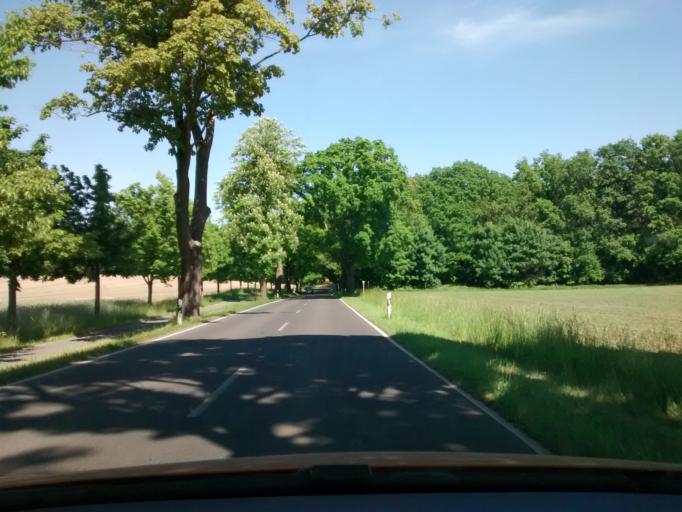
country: DE
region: Brandenburg
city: Diensdorf-Radlow
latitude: 52.2727
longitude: 14.0318
